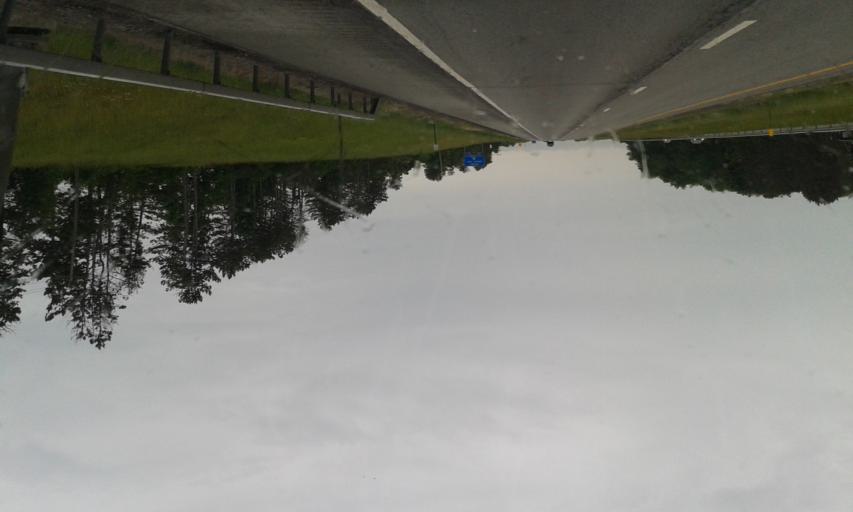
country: US
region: New York
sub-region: Genesee County
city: Bergen
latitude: 43.0302
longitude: -77.8978
